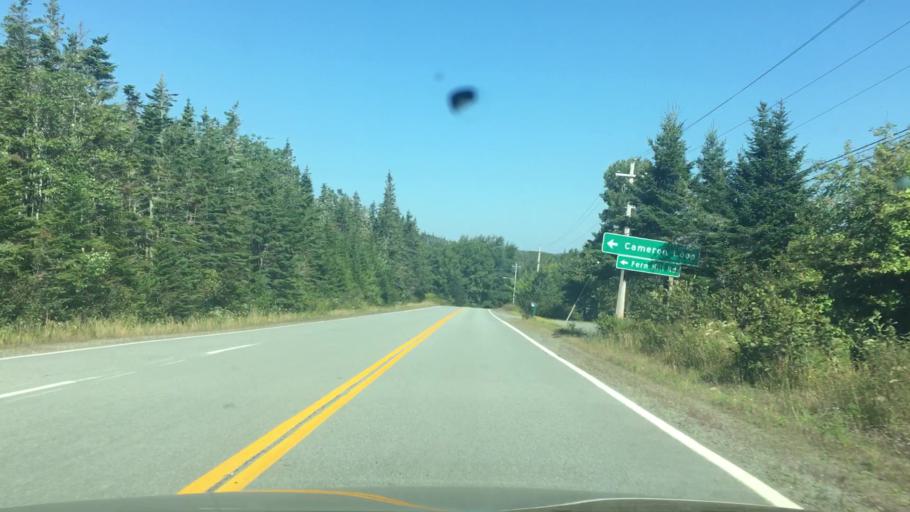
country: CA
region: Nova Scotia
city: New Glasgow
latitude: 44.8191
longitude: -62.6339
